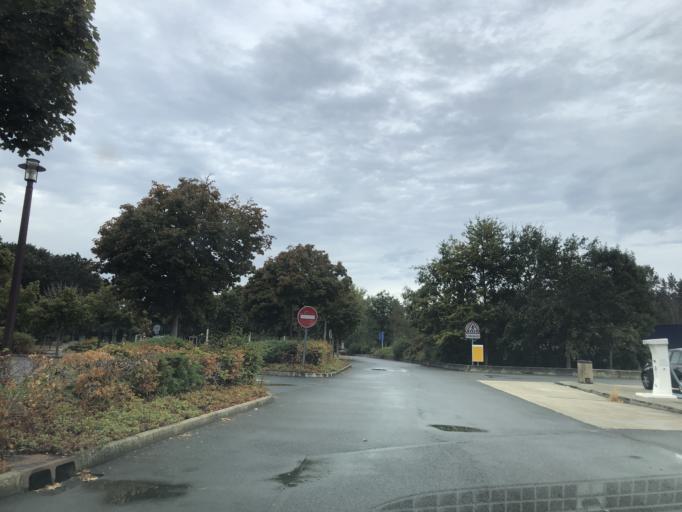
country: FR
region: Ile-de-France
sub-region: Departement de Seine-et-Marne
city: Montereau-Fault-Yonne
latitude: 48.4290
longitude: 2.9318
